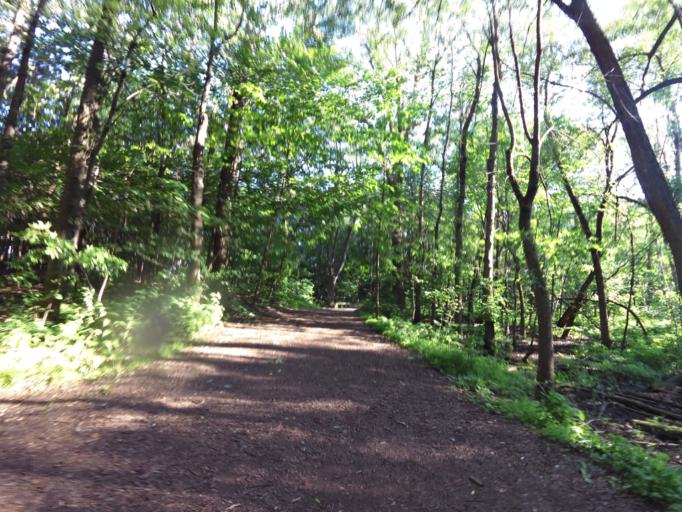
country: CA
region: Quebec
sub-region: Montreal
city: Montreal
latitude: 45.5026
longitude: -73.5882
